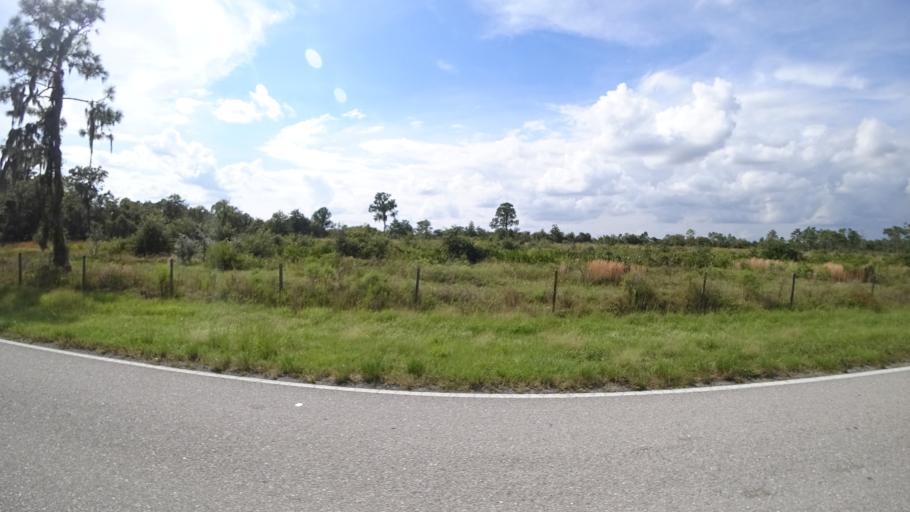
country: US
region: Florida
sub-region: Hillsborough County
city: Wimauma
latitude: 27.5426
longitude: -82.1040
